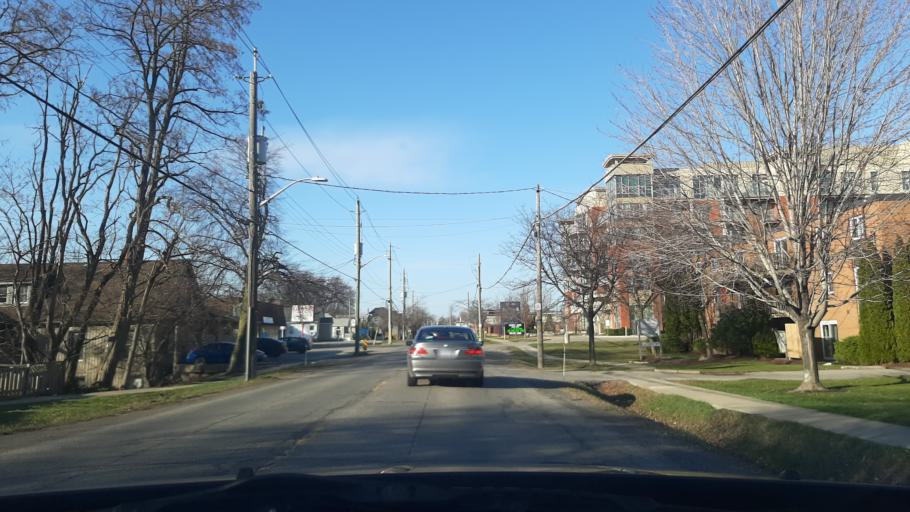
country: CA
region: Ontario
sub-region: Regional Municipality of Niagara
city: St. Catharines
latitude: 43.1934
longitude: -79.2609
